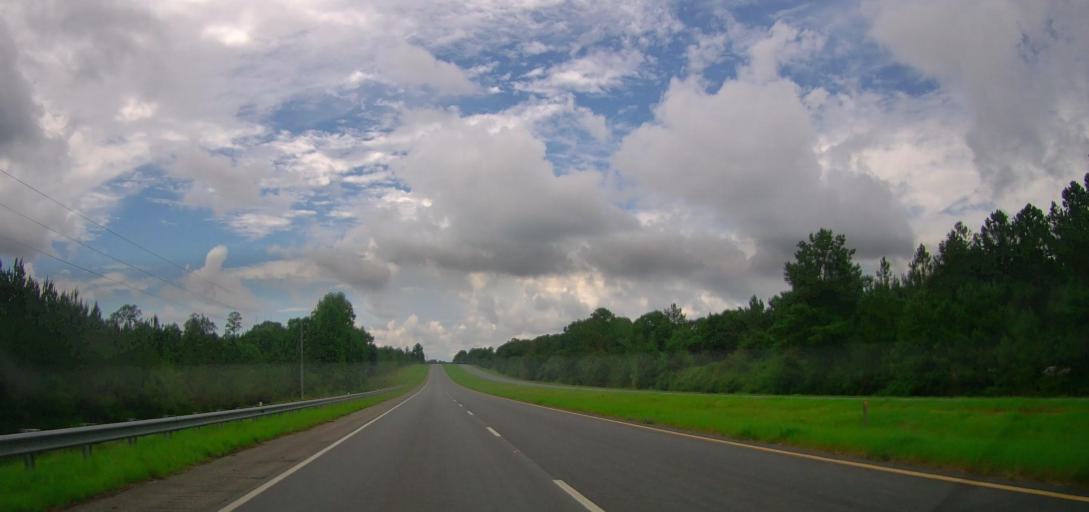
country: US
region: Georgia
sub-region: Dodge County
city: Eastman
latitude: 32.1145
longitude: -83.1021
